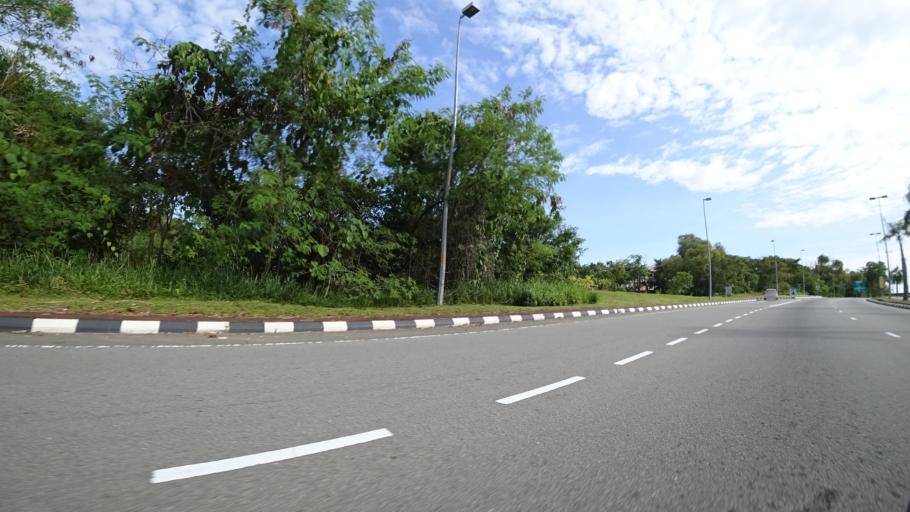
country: BN
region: Brunei and Muara
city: Bandar Seri Begawan
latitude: 4.8967
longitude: 114.9140
